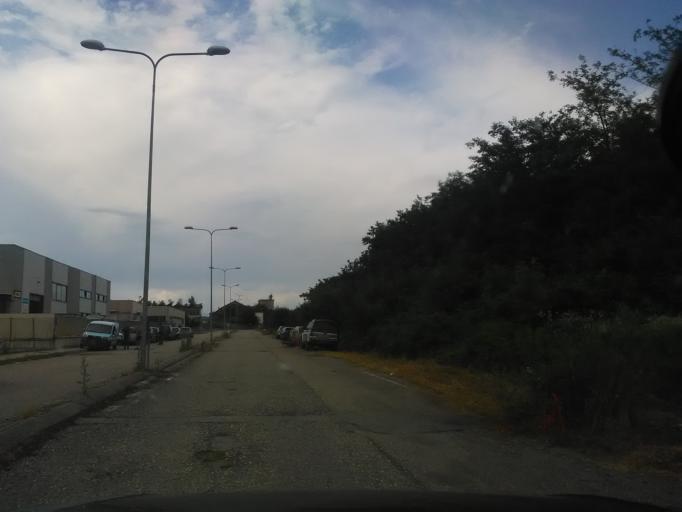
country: IT
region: Piedmont
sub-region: Provincia di Vercelli
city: Gattinara
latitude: 45.6050
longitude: 8.3649
